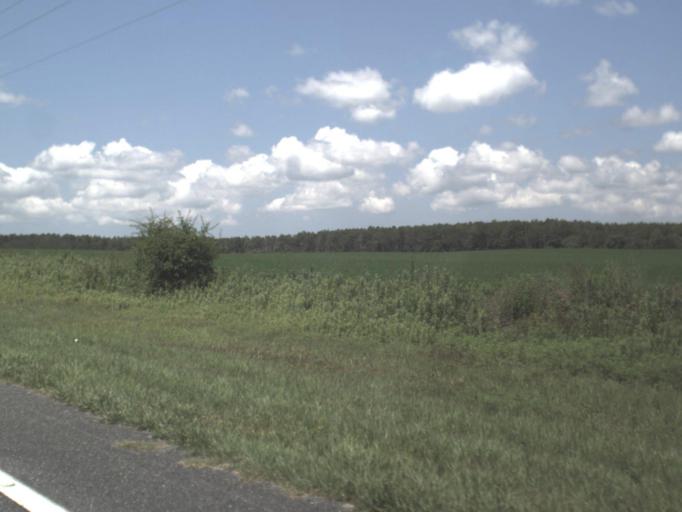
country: US
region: Florida
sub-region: Levy County
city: Williston Highlands
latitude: 29.2554
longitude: -82.5507
